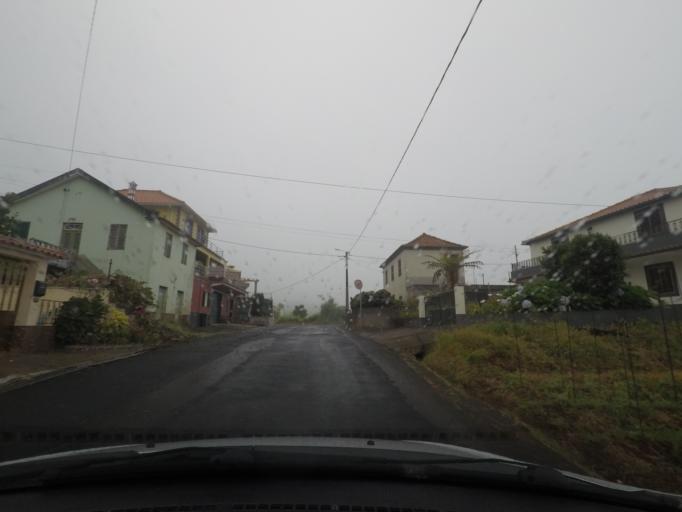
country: PT
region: Madeira
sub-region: Santana
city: Santana
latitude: 32.7948
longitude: -16.8749
